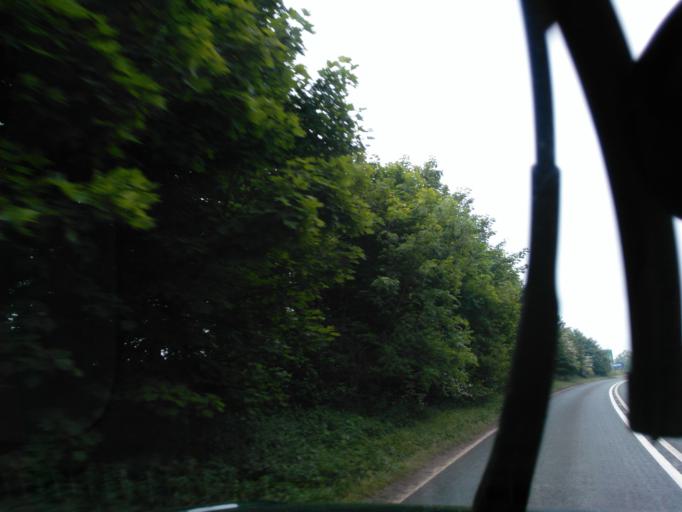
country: GB
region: England
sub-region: Somerset
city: Bruton
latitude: 51.1924
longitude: -2.4265
